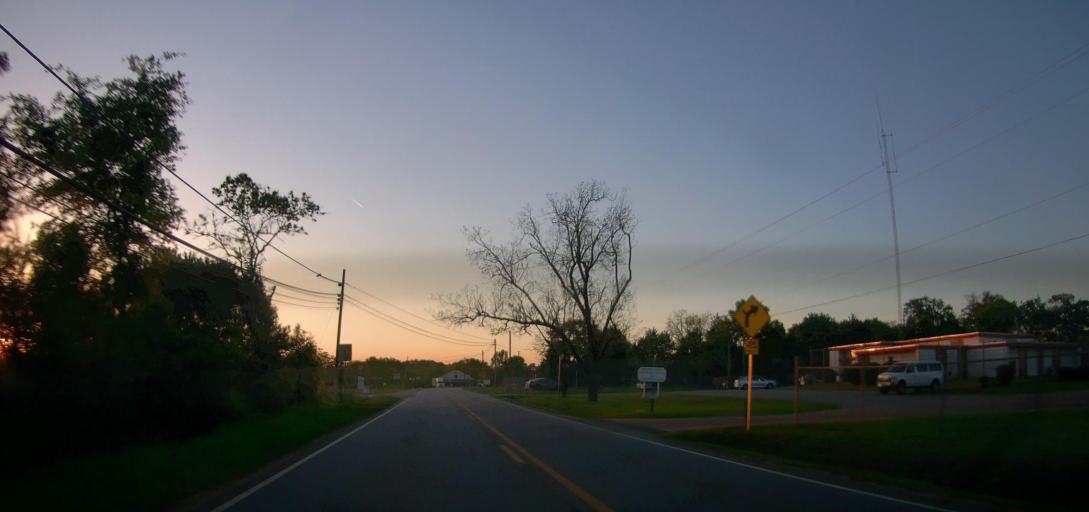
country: US
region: Georgia
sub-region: Marion County
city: Buena Vista
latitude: 32.3306
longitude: -84.5276
